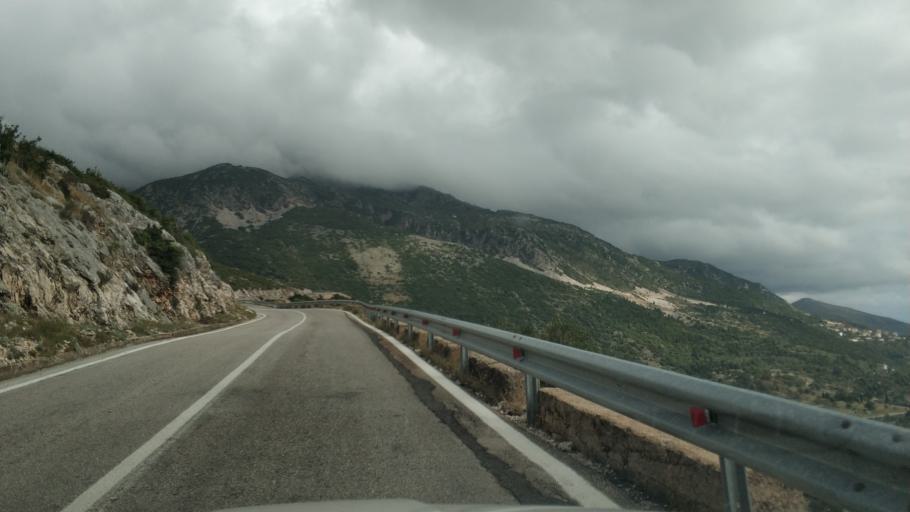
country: AL
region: Vlore
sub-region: Rrethi i Vlores
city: Vranisht
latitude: 40.1798
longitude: 19.5997
